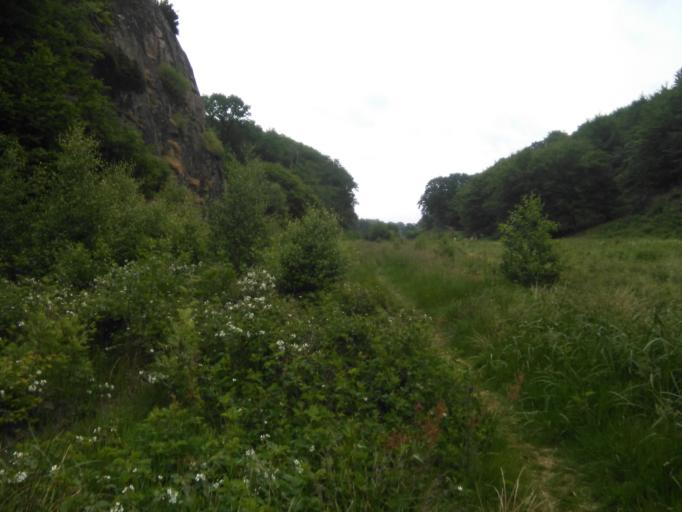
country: DK
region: Capital Region
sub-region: Bornholm Kommune
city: Akirkeby
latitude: 55.1080
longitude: 14.8993
